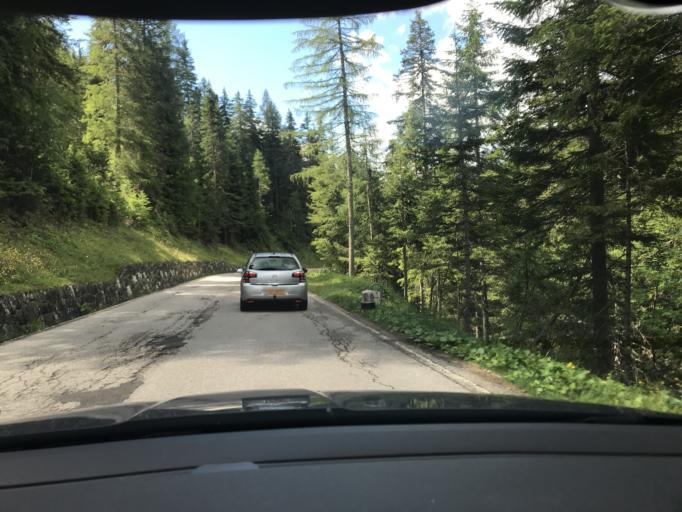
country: IT
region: Veneto
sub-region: Provincia di Belluno
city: Livinallongo del Col di Lana
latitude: 46.5028
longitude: 11.9919
